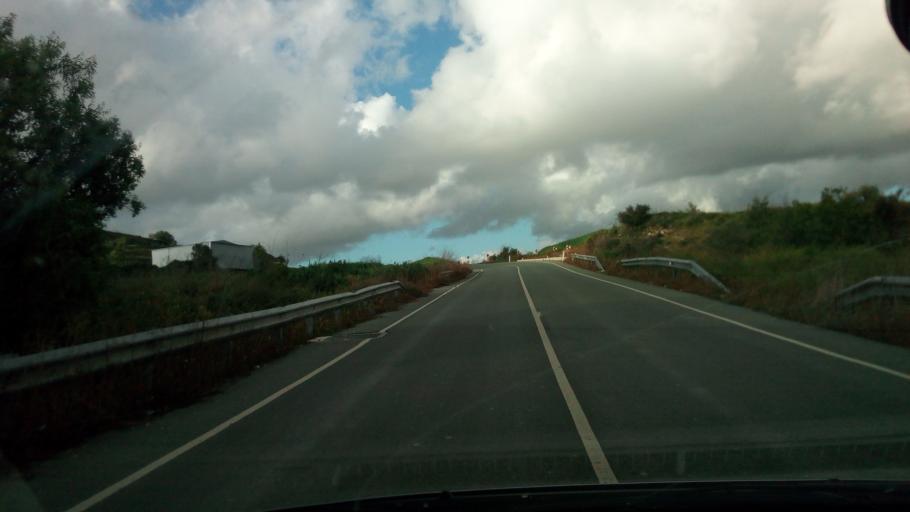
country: CY
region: Pafos
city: Mesogi
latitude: 34.8609
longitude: 32.5036
